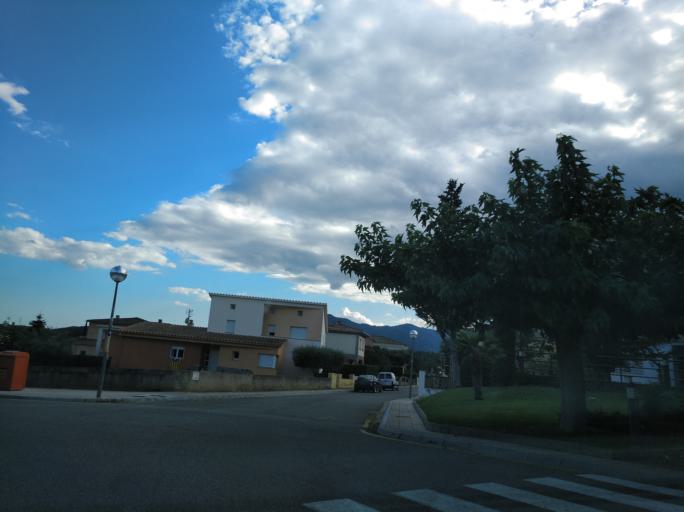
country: ES
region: Catalonia
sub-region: Provincia de Girona
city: Angles
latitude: 41.9704
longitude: 2.6640
